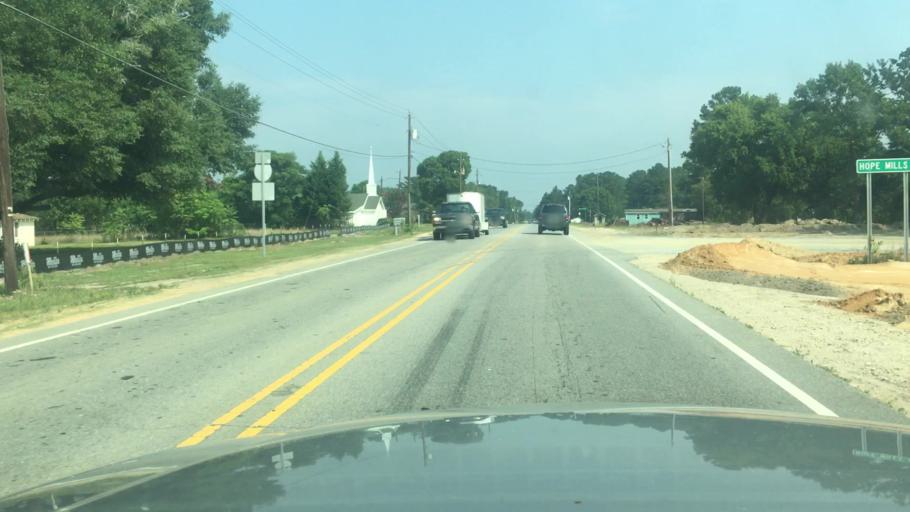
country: US
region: North Carolina
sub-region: Cumberland County
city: Hope Mills
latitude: 34.9471
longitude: -78.9329
